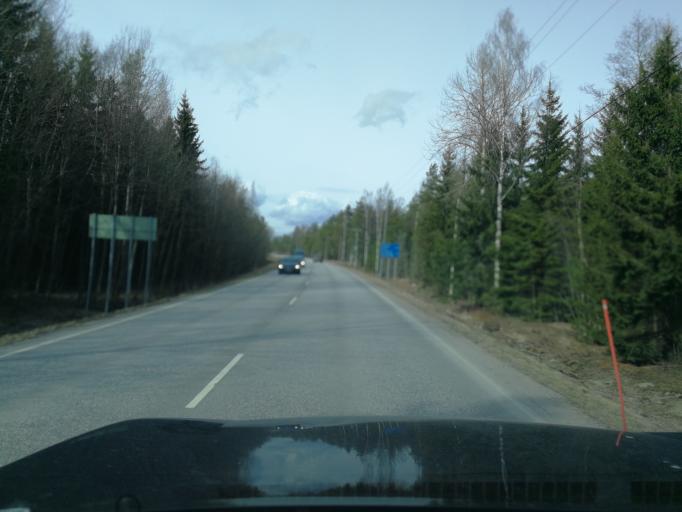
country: FI
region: Uusimaa
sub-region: Helsinki
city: Siuntio
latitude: 60.0986
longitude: 24.2513
